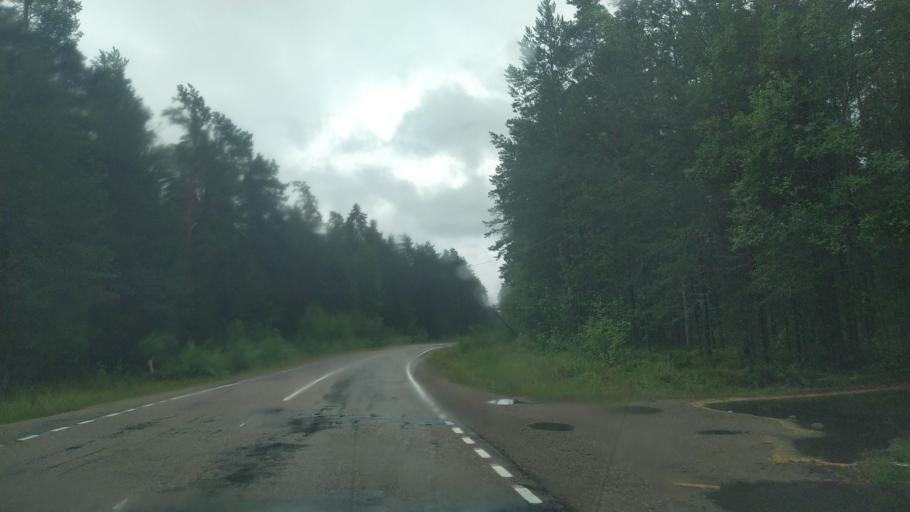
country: RU
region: Leningrad
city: Priozersk
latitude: 60.9707
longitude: 30.2838
